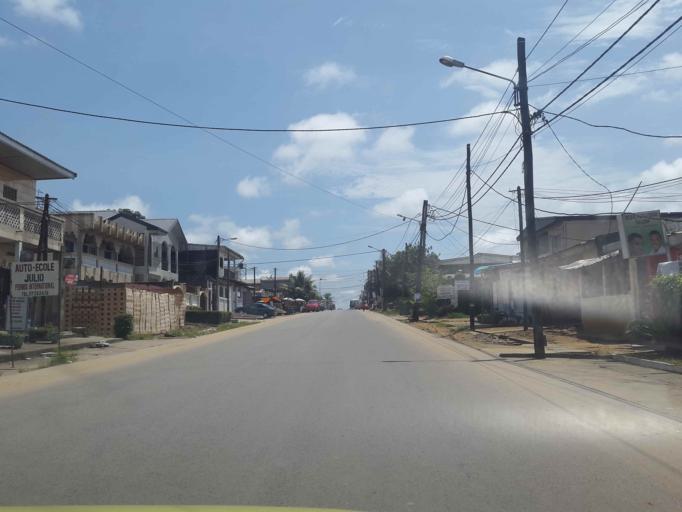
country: CM
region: Littoral
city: Douala
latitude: 4.0900
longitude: 9.7466
